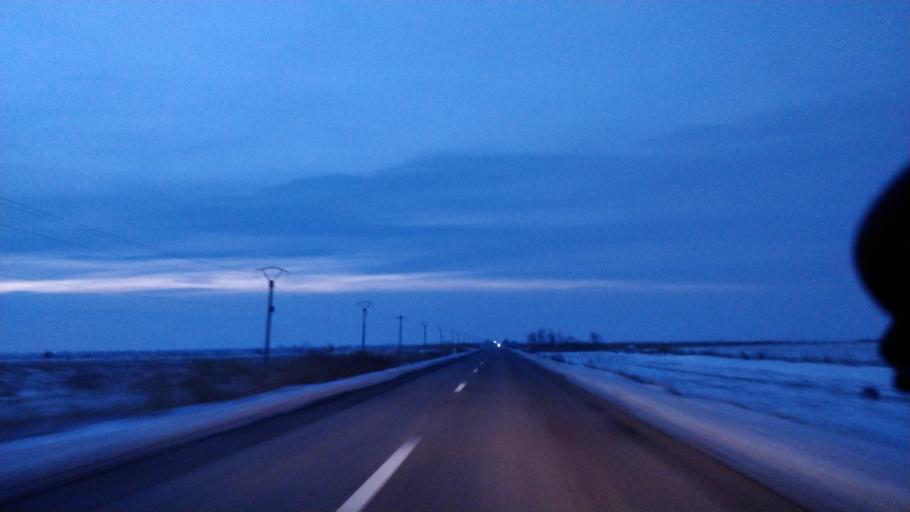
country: RO
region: Vrancea
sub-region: Comuna Vulturu
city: Vadu Rosca
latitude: 45.6002
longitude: 27.4599
